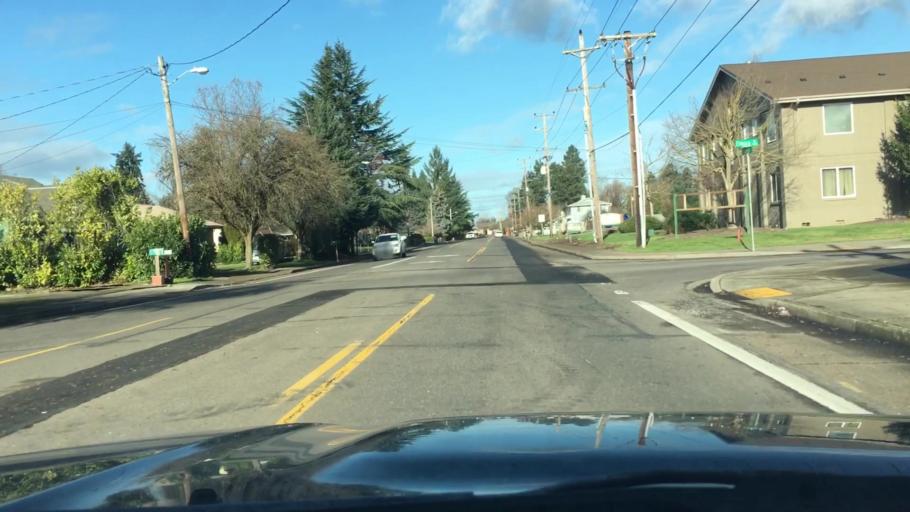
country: US
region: Oregon
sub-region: Lane County
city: Eugene
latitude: 44.0661
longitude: -123.1631
